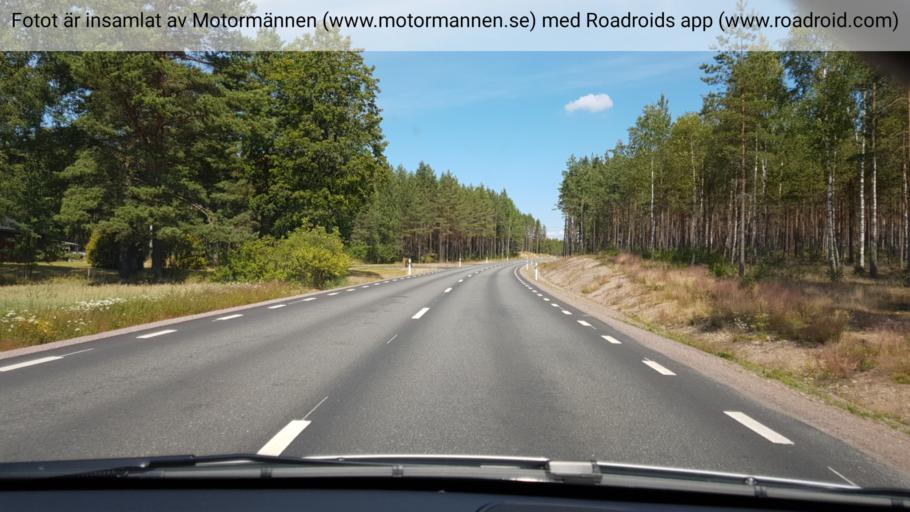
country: SE
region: Vaestra Goetaland
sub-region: Tibro Kommun
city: Tibro
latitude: 58.4632
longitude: 14.1762
